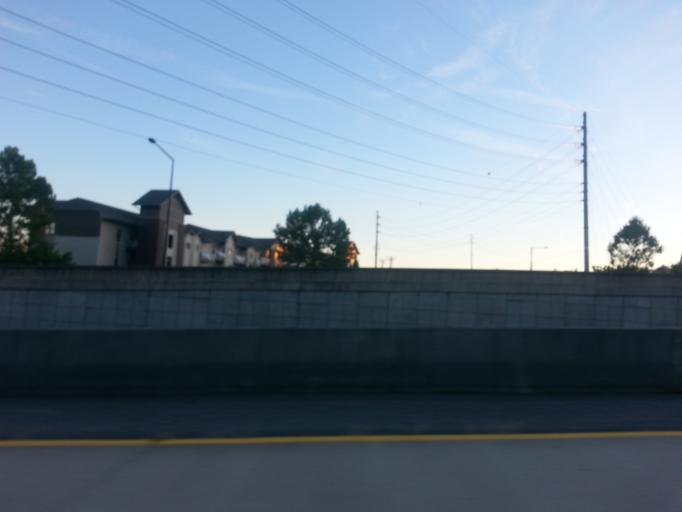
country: US
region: Tennessee
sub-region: Knox County
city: Knoxville
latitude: 35.9659
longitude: -83.9057
